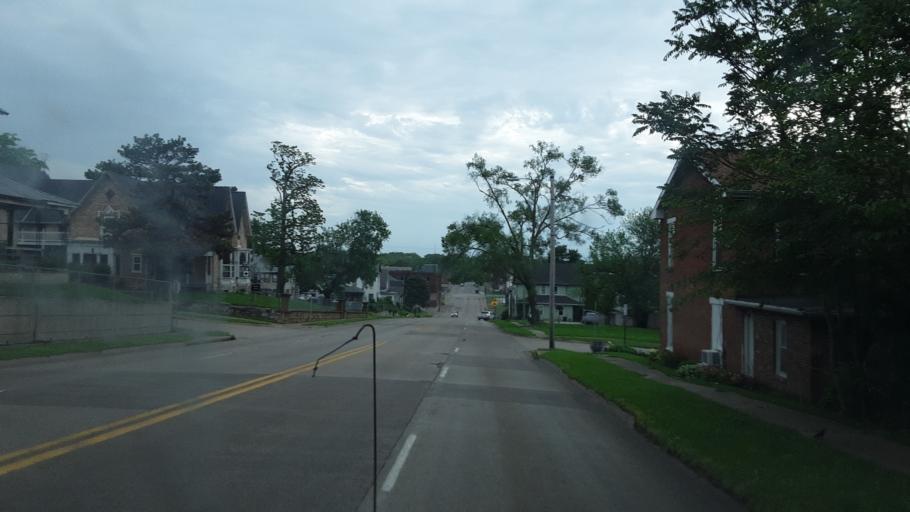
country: US
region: Iowa
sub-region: Lee County
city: Keokuk
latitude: 40.3951
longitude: -91.3886
